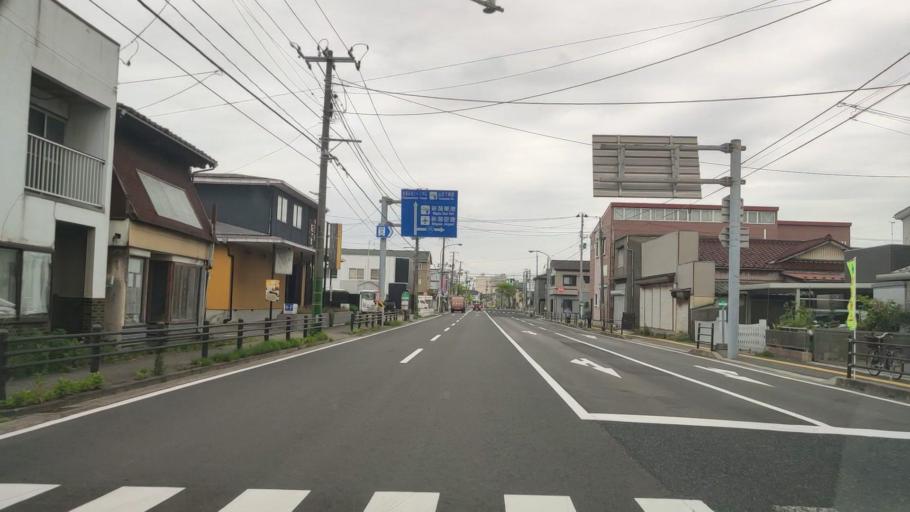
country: JP
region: Niigata
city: Niigata-shi
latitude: 37.9363
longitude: 139.0723
